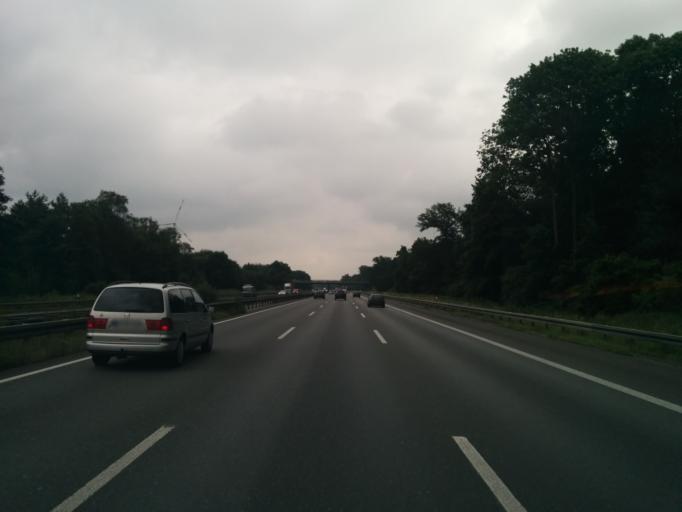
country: DE
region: North Rhine-Westphalia
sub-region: Regierungsbezirk Detmold
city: Guetersloh
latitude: 51.8712
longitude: 8.3984
